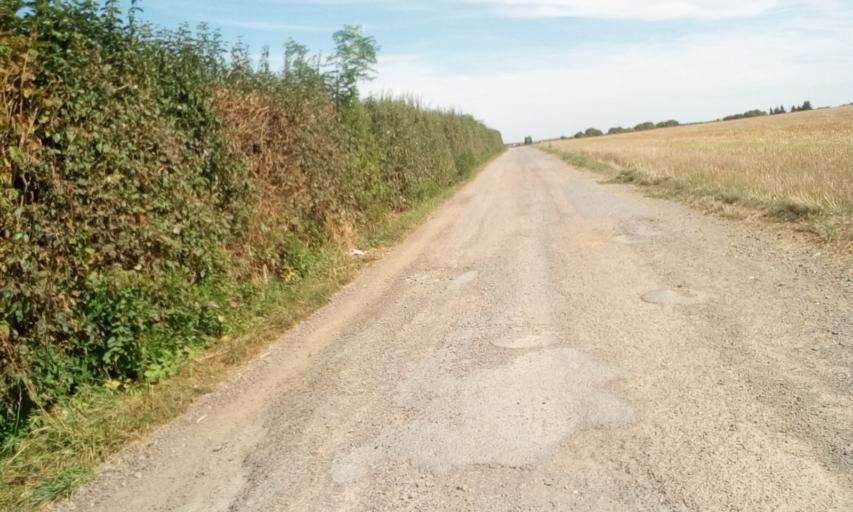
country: FR
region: Lower Normandy
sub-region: Departement du Calvados
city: Bretteville-sur-Odon
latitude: 49.1531
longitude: -0.4097
